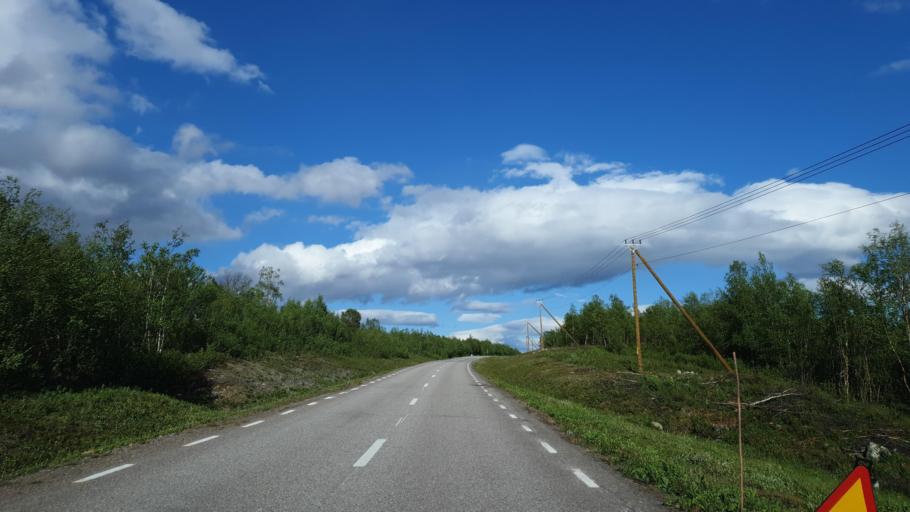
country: SE
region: Norrbotten
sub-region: Kiruna Kommun
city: Kiruna
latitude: 67.8746
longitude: 19.1878
